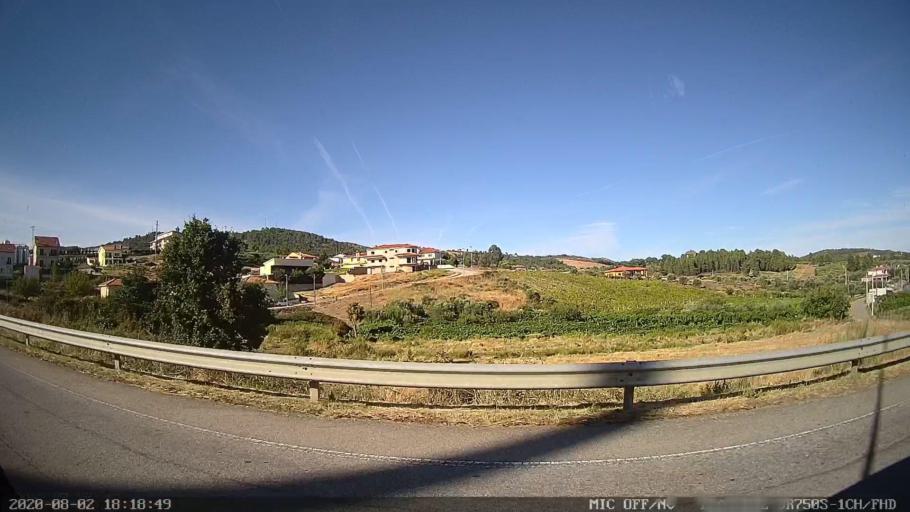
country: PT
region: Vila Real
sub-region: Murca
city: Murca
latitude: 41.4041
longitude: -7.4481
